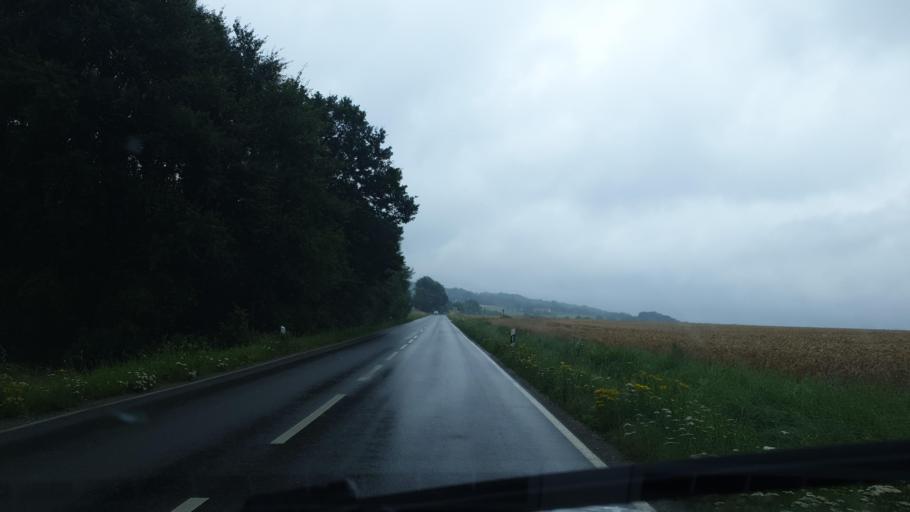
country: DE
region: North Rhine-Westphalia
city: Loehne
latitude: 52.1659
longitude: 8.6831
